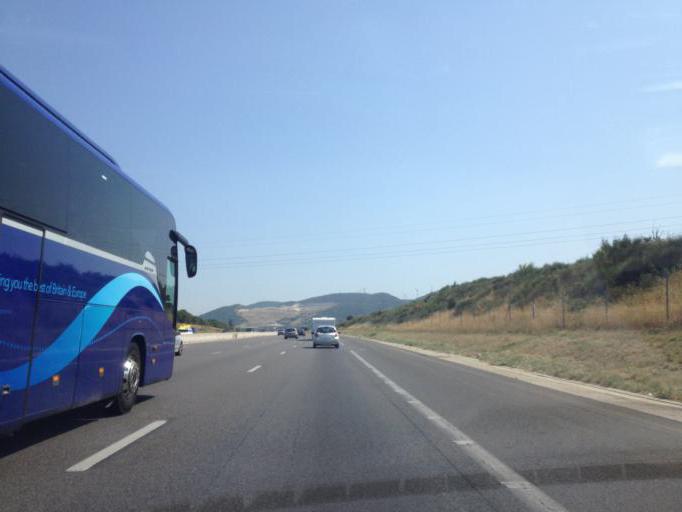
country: FR
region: Rhone-Alpes
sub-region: Departement de la Drome
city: Donzere
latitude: 44.4327
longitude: 4.7448
